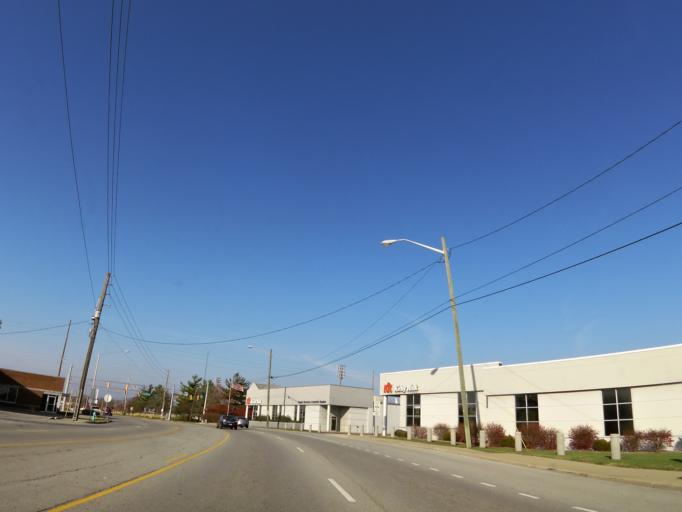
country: US
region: Indiana
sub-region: Marion County
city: Indianapolis
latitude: 39.7889
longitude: -86.1859
